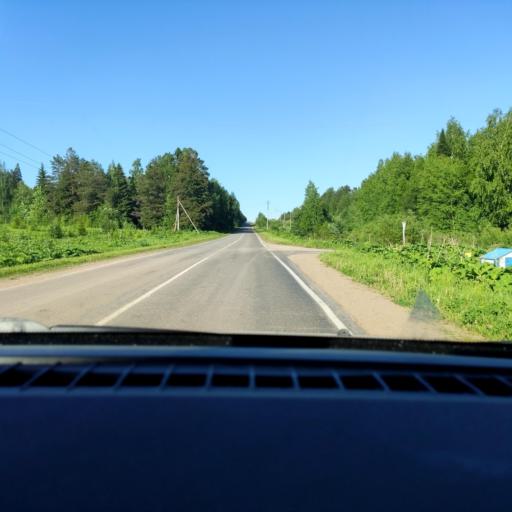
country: RU
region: Perm
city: Overyata
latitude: 58.1272
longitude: 55.8738
